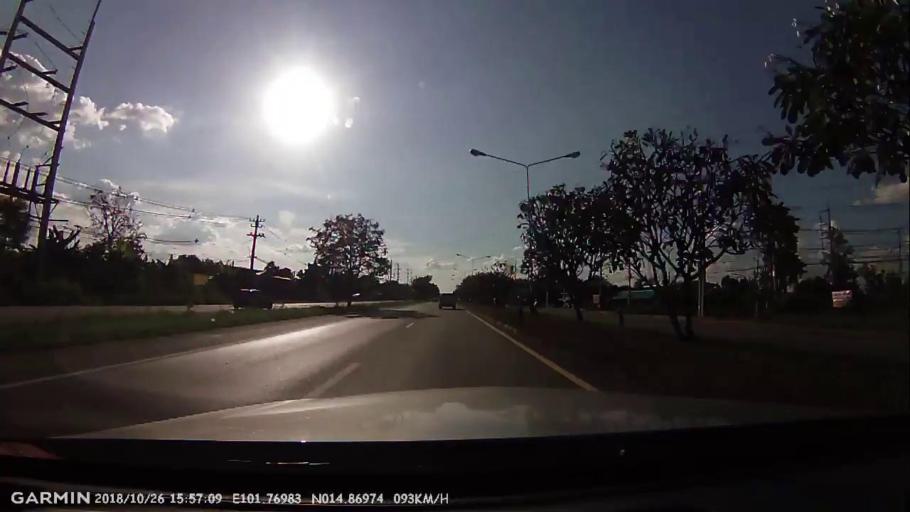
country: TH
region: Nakhon Ratchasima
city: Sikhio
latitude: 14.8698
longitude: 101.7694
